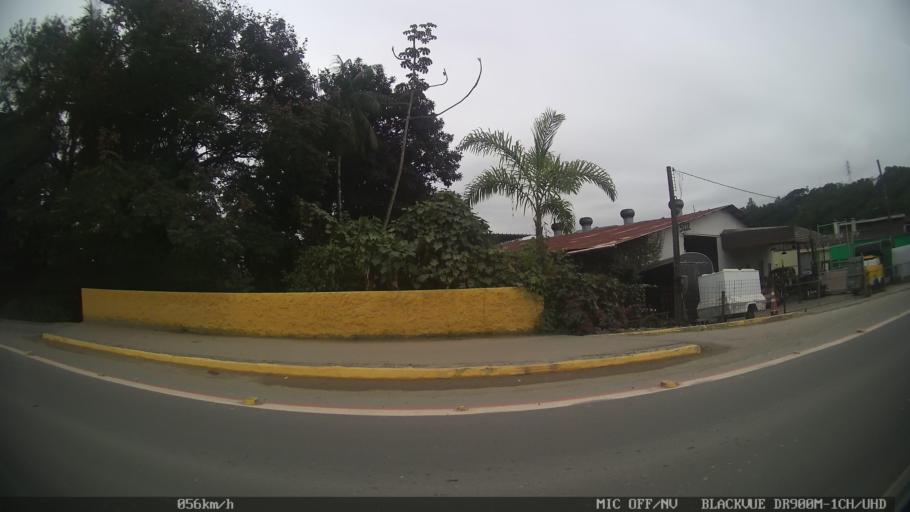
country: BR
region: Santa Catarina
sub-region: Joinville
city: Joinville
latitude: -26.2880
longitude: -48.8967
